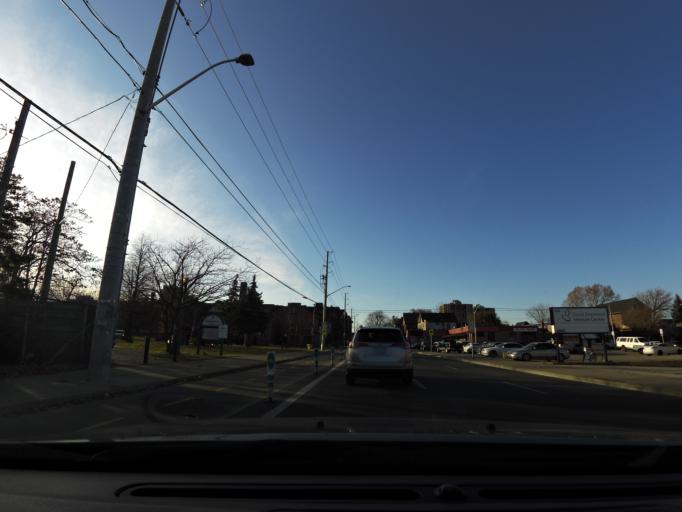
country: CA
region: Ontario
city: Hamilton
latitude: 43.2590
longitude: -79.8602
